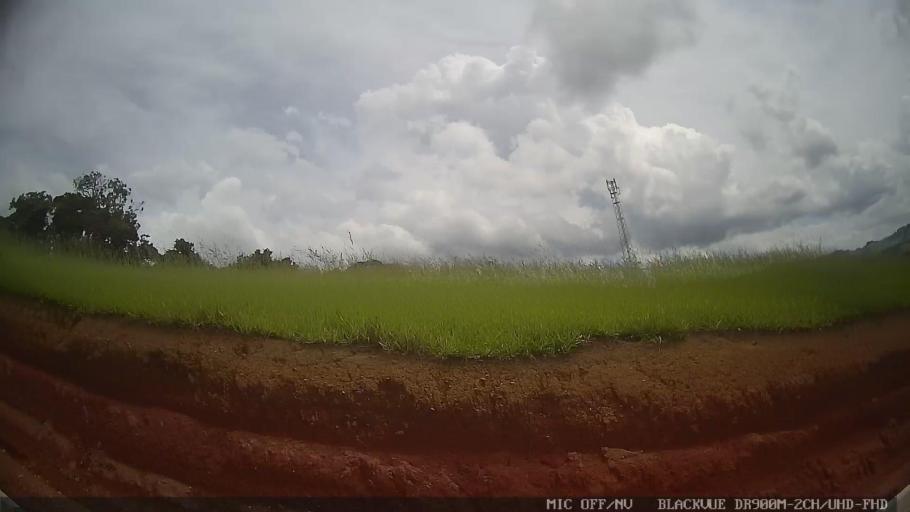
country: BR
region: Minas Gerais
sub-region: Extrema
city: Extrema
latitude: -22.7390
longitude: -46.3757
